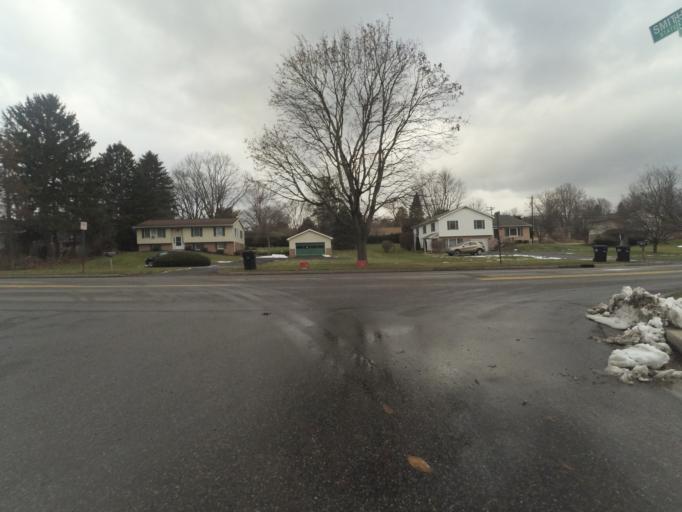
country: US
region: Pennsylvania
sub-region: Centre County
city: State College
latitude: 40.7933
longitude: -77.8455
